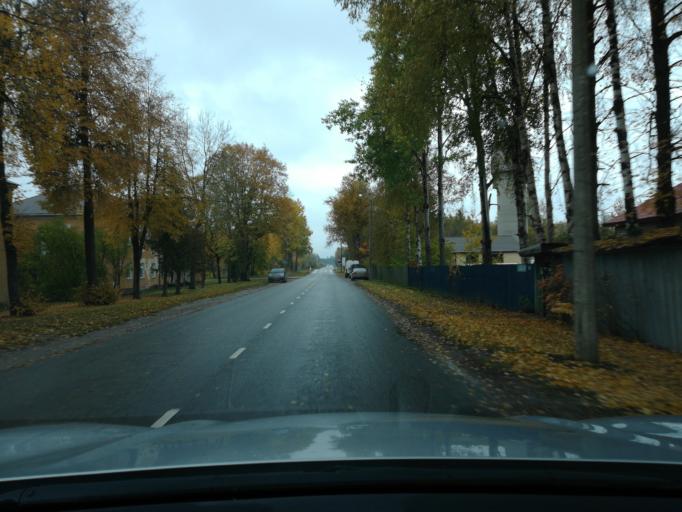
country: EE
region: Ida-Virumaa
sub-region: Johvi vald
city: Johvi
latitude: 59.3094
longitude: 27.4564
